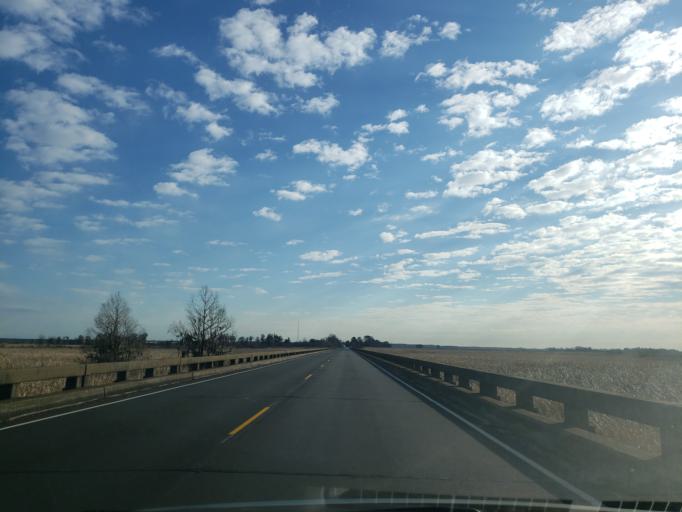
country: US
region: Georgia
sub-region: Chatham County
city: Port Wentworth
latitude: 32.1659
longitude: -81.1294
